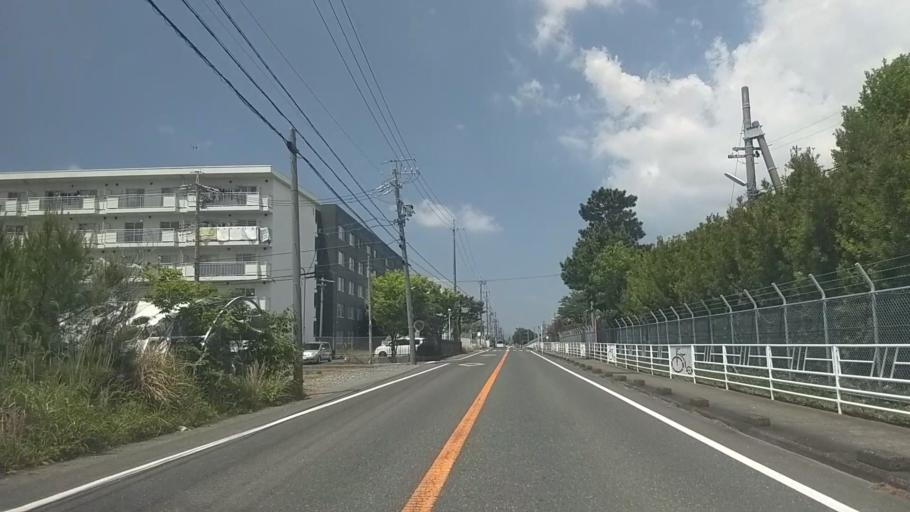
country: JP
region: Shizuoka
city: Hamamatsu
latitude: 34.7423
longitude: 137.6931
